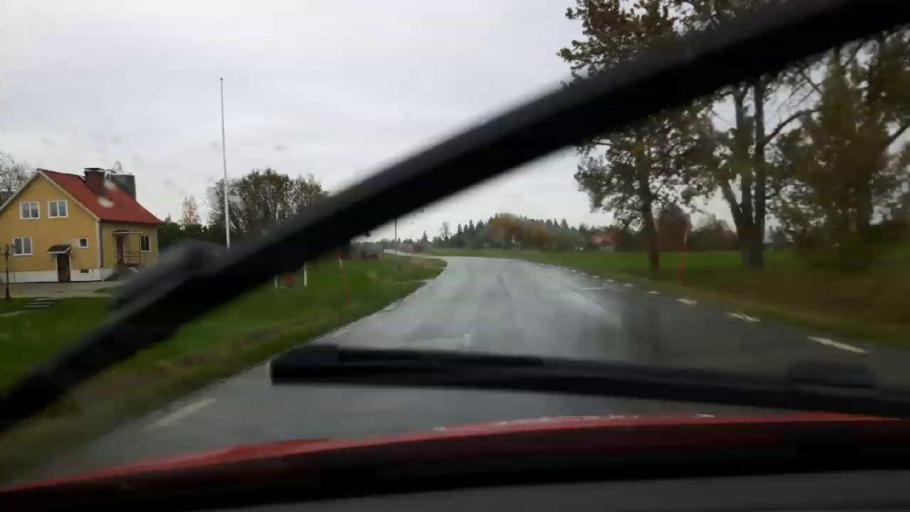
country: SE
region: Jaemtland
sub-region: Bergs Kommun
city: Hoverberg
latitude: 63.0359
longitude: 14.3454
